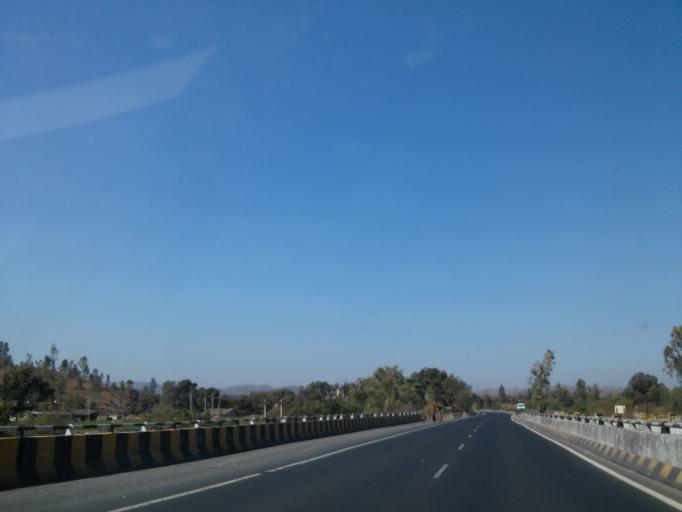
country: IN
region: Gujarat
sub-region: Sabar Kantha
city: Meghraj
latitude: 23.7409
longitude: 73.4305
